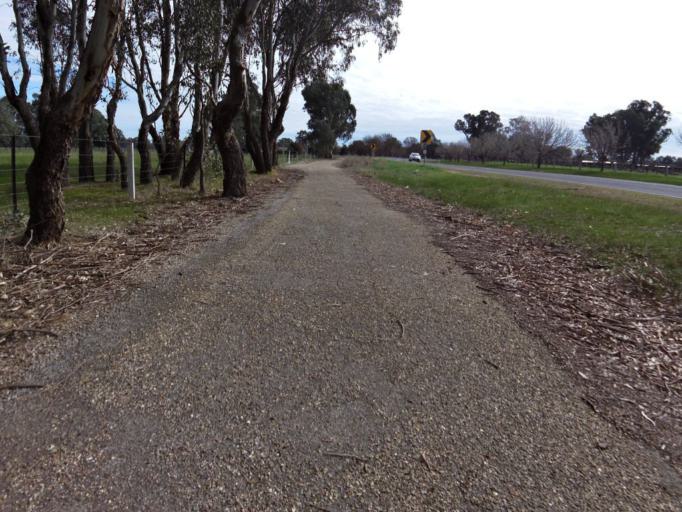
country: AU
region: Victoria
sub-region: Wangaratta
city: Wangaratta
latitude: -36.4364
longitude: 146.3585
